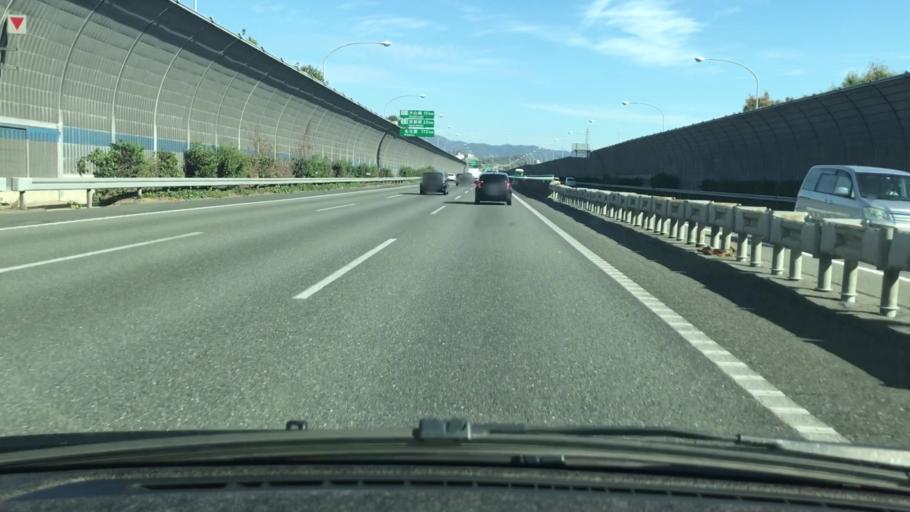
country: JP
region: Osaka
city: Ibaraki
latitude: 34.8355
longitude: 135.5640
